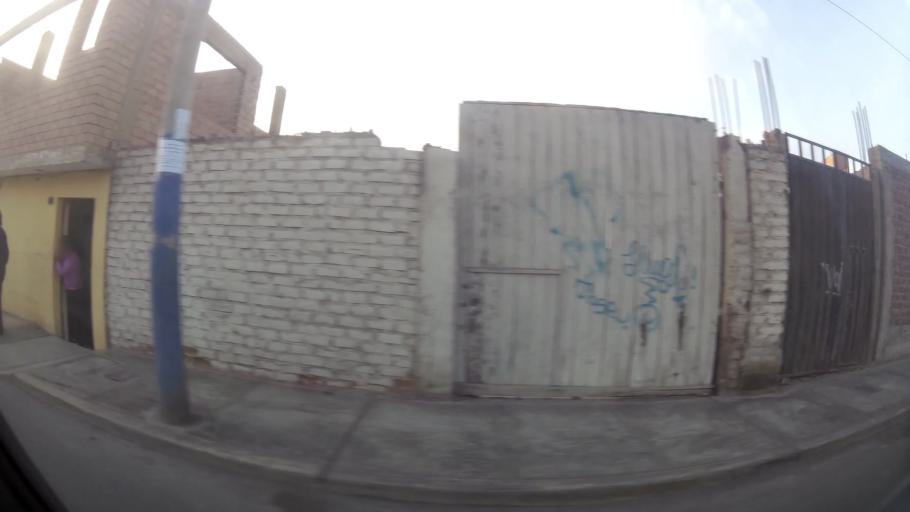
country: PE
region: Lima
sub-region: Huaura
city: Huacho
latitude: -11.1102
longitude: -77.6019
